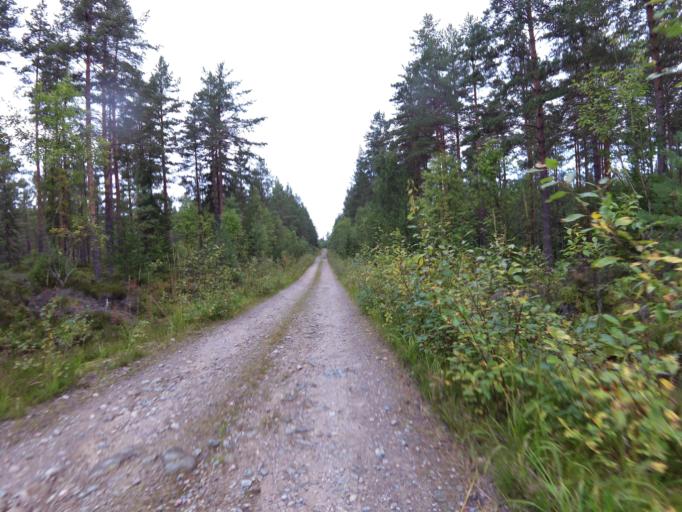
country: SE
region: Gaevleborg
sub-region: Gavle Kommun
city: Valbo
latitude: 60.7449
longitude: 16.9828
